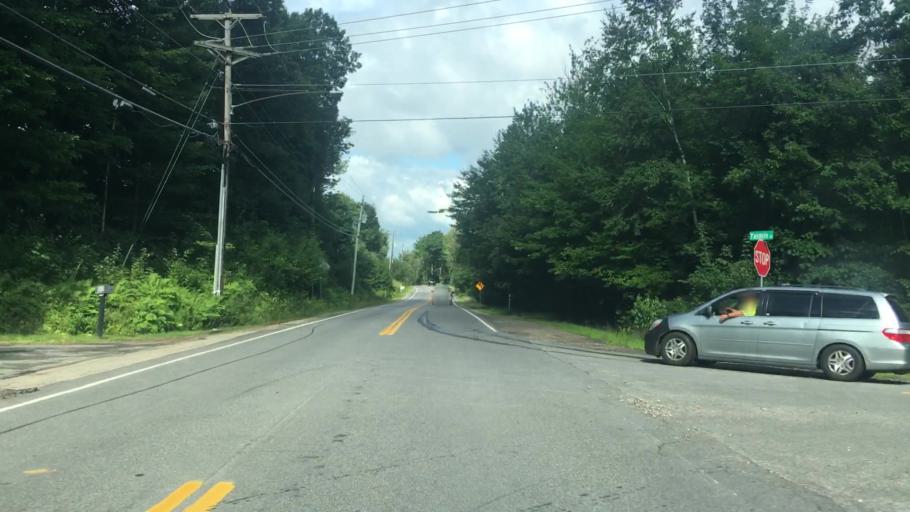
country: US
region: New Hampshire
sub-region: Belknap County
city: Gilford
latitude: 43.5636
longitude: -71.3759
